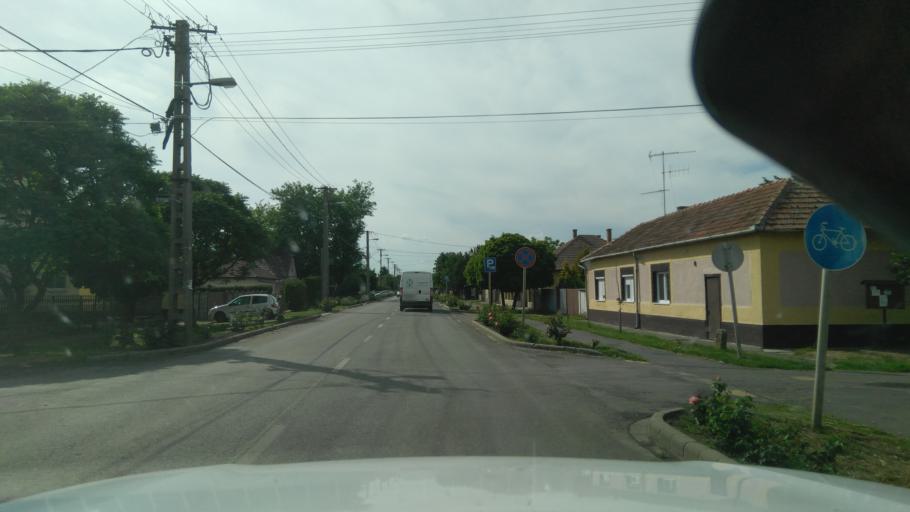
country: HU
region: Bekes
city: Medgyesegyhaza
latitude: 46.5016
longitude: 21.0204
